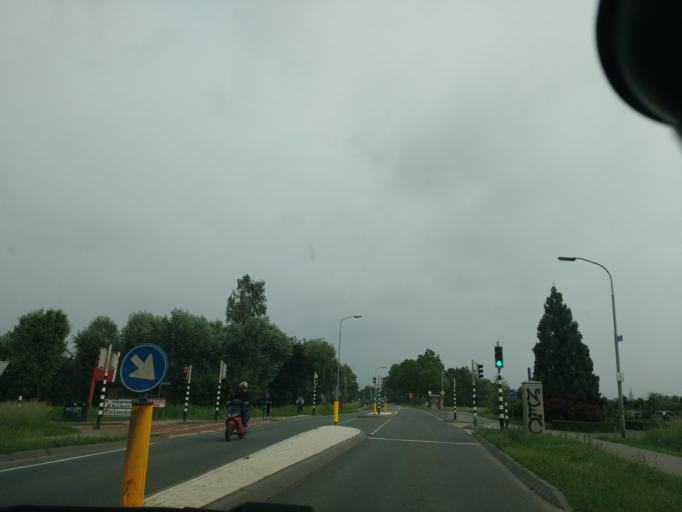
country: NL
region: Gelderland
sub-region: Gemeente Nijmegen
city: Nijmegen
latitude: 51.8689
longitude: 5.8547
